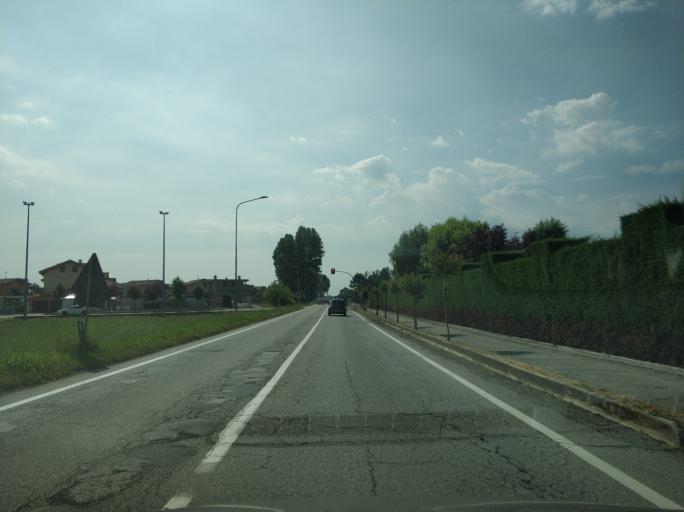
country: IT
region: Piedmont
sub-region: Provincia di Torino
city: Marocchi
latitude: 44.9415
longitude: 7.8179
